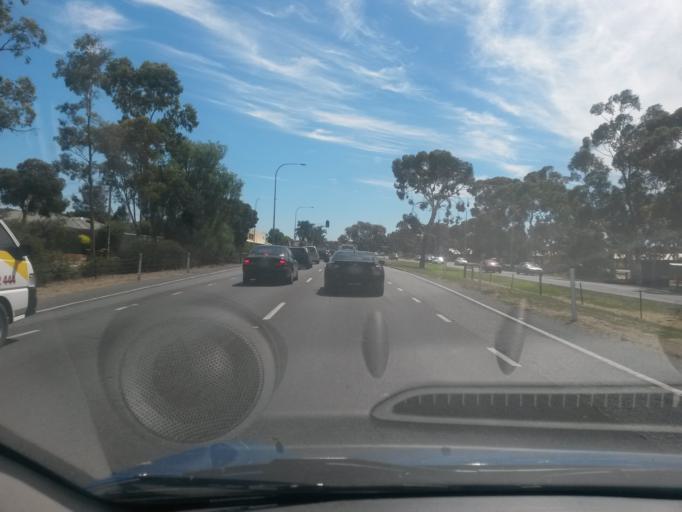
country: AU
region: South Australia
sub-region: Salisbury
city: Salisbury
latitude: -34.7756
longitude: 138.6610
